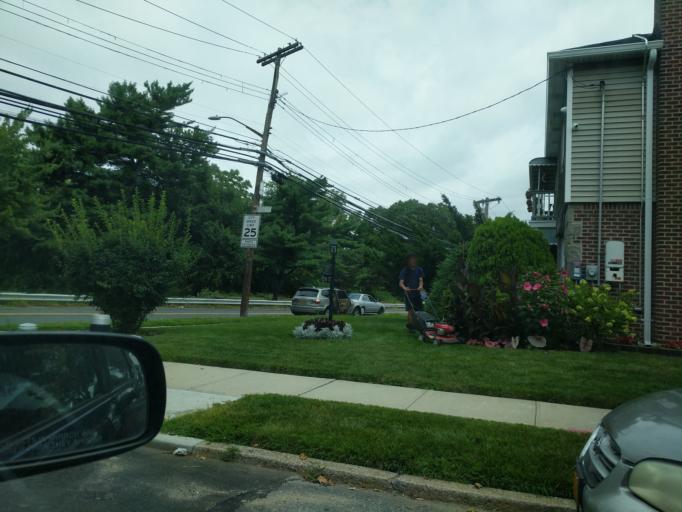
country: US
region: New York
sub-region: Nassau County
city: South Valley Stream
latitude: 40.6759
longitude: -73.7315
